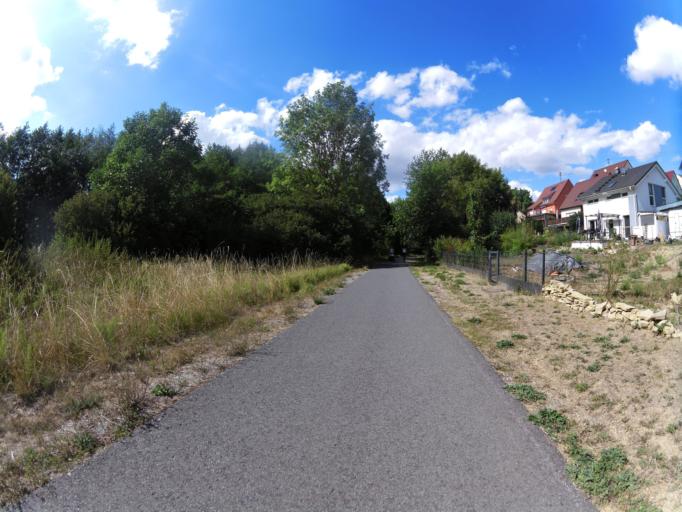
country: DE
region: Bavaria
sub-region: Regierungsbezirk Unterfranken
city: Gaukonigshofen
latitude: 49.6299
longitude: 10.0067
